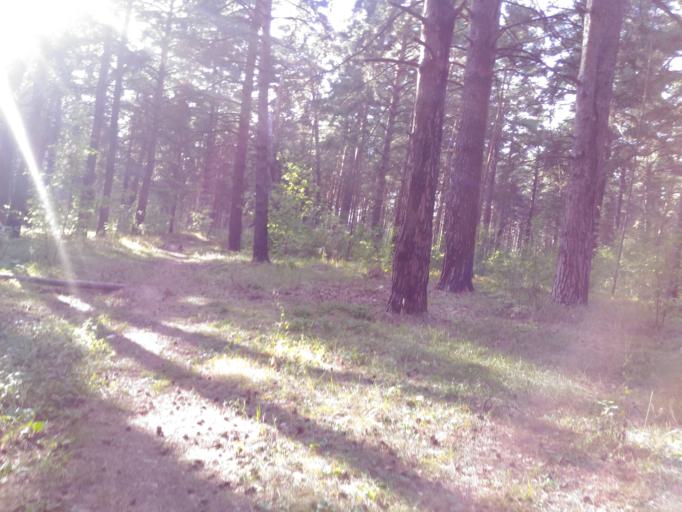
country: RU
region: Ulyanovsk
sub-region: Ulyanovskiy Rayon
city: Ulyanovsk
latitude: 54.3539
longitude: 48.5207
